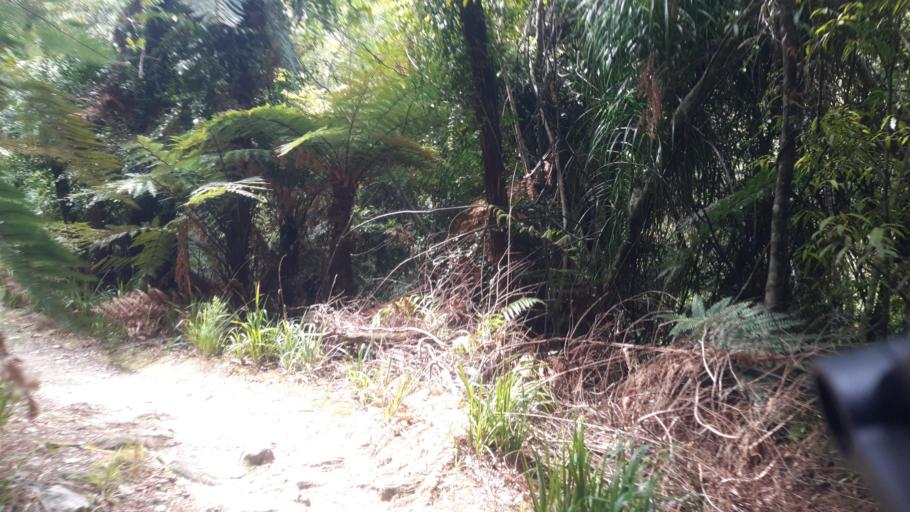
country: NZ
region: Marlborough
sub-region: Marlborough District
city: Picton
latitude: -41.2459
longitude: 173.9568
